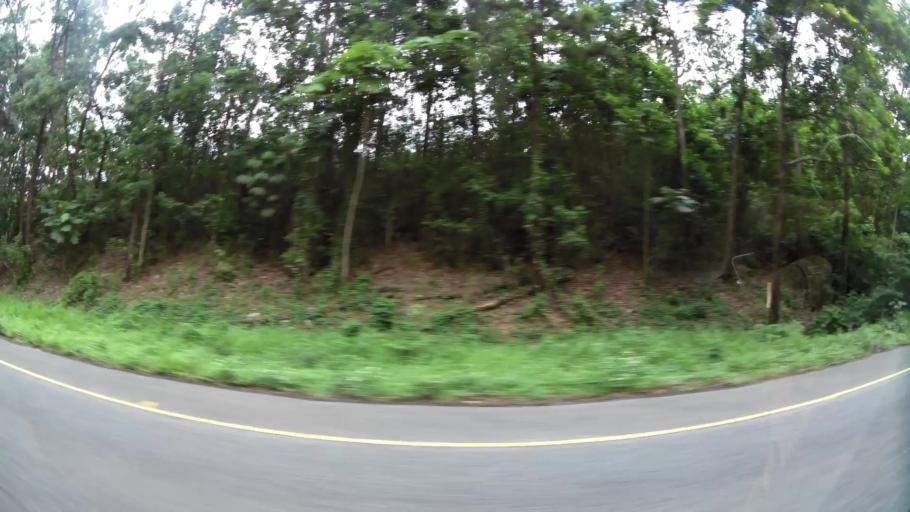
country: DO
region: Monsenor Nouel
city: Piedra Blanca
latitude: 18.8082
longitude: -70.2797
